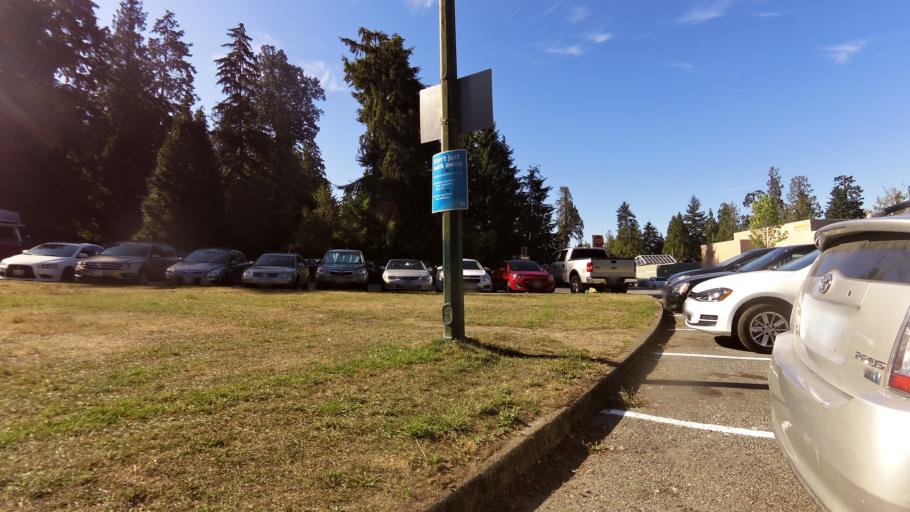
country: CA
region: British Columbia
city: West End
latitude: 49.3011
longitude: -123.1299
